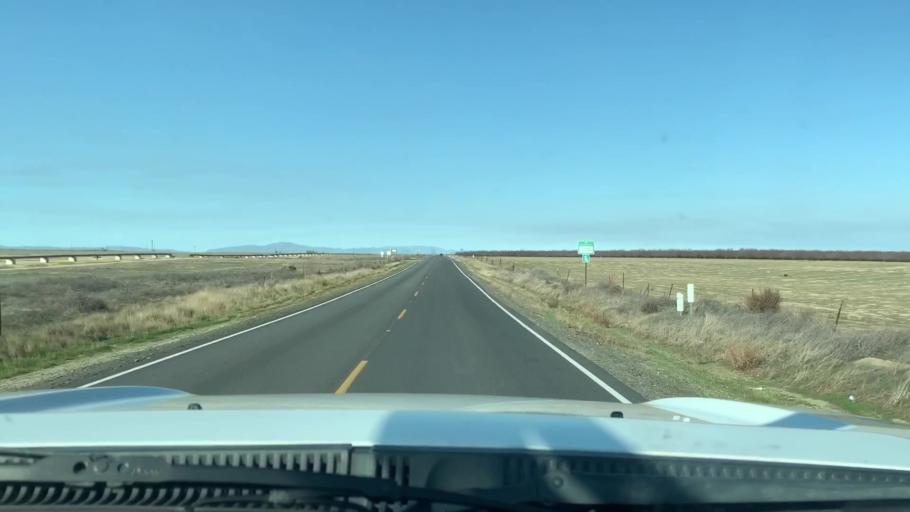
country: US
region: California
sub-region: Kern County
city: Lost Hills
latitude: 35.5528
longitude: -119.7912
